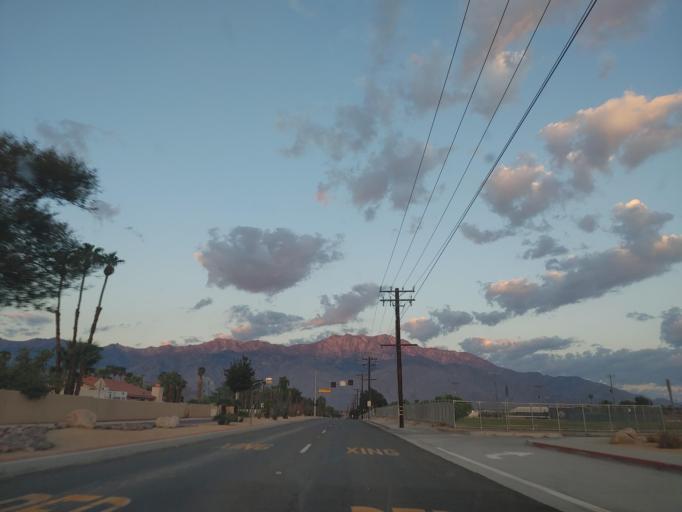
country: US
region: California
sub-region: Riverside County
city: Cathedral City
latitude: 33.8015
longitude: -116.4505
